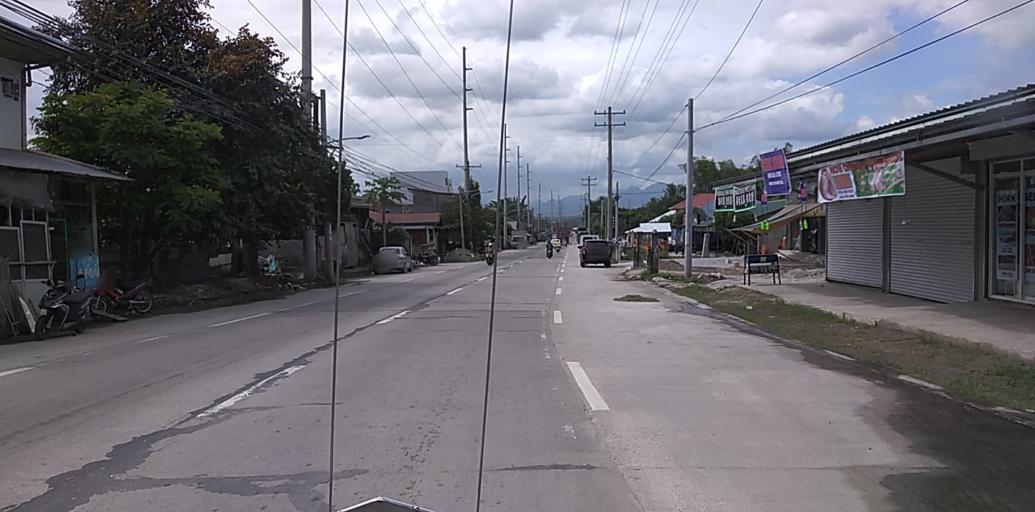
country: PH
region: Central Luzon
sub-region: Province of Pampanga
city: Pio
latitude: 15.0493
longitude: 120.5303
